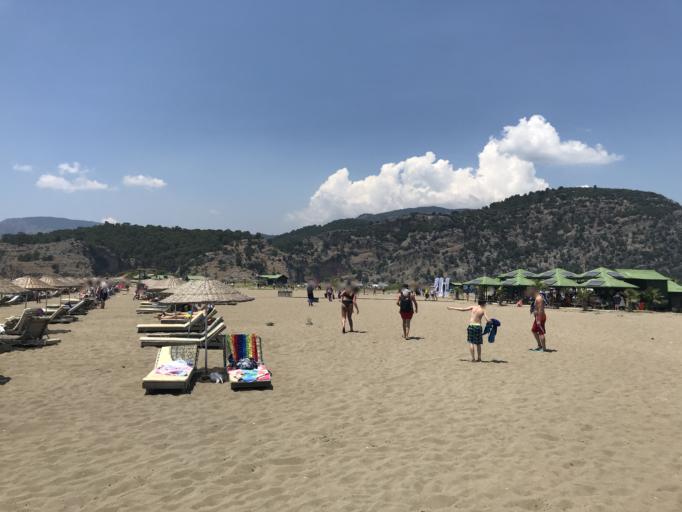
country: TR
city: Dalyan
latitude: 36.7996
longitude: 28.6086
